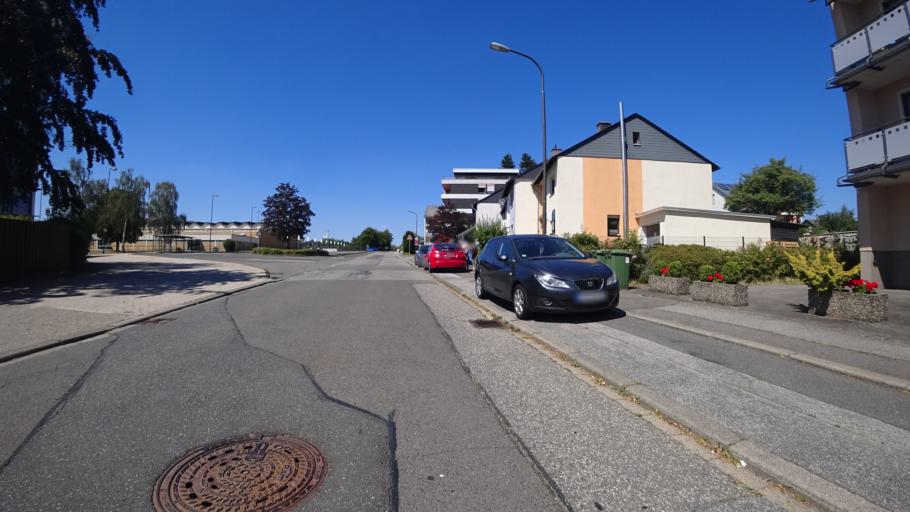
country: DE
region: Rheinland-Pfalz
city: Kumbdchen
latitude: 49.9885
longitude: 7.5183
